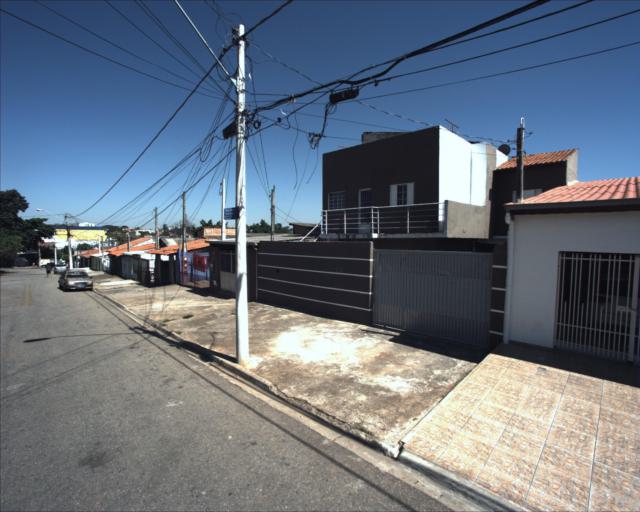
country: BR
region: Sao Paulo
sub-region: Sorocaba
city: Sorocaba
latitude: -23.4671
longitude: -47.4885
